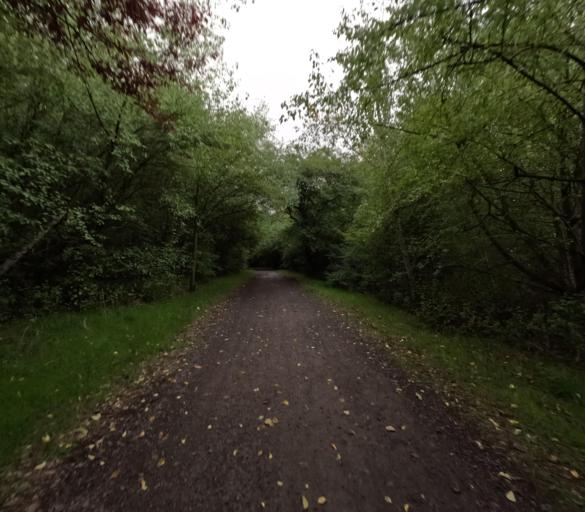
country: DE
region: Saxony
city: Markranstadt
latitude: 51.2944
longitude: 12.2233
